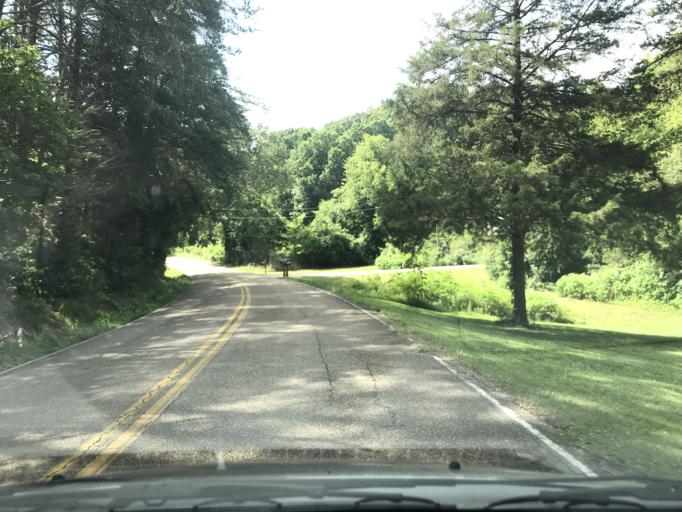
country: US
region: Tennessee
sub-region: Hamilton County
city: Lakesite
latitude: 35.1784
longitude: -85.0652
